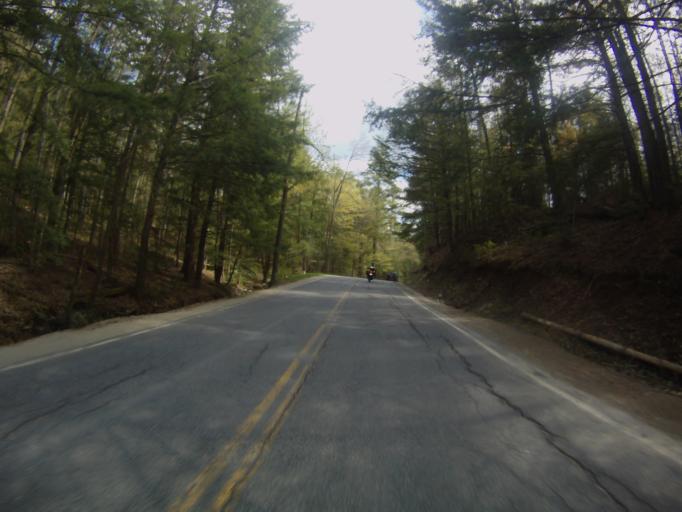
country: US
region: New York
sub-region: Essex County
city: Mineville
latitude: 43.9960
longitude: -73.6587
